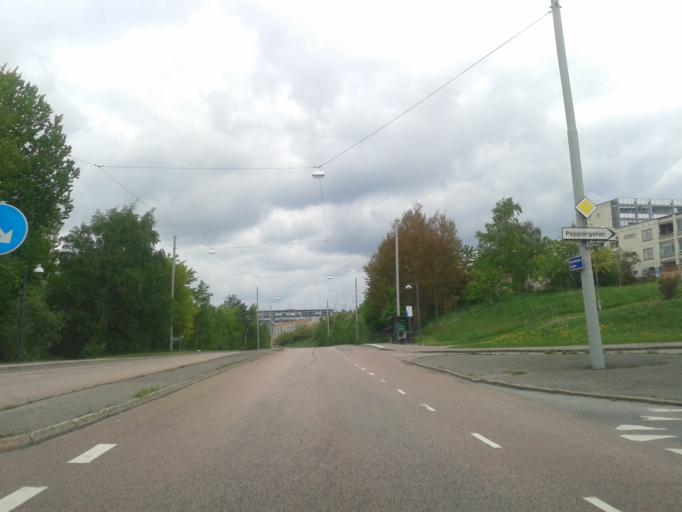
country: SE
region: Vaestra Goetaland
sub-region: Goteborg
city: Gardsten
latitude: 57.8006
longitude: 12.0241
